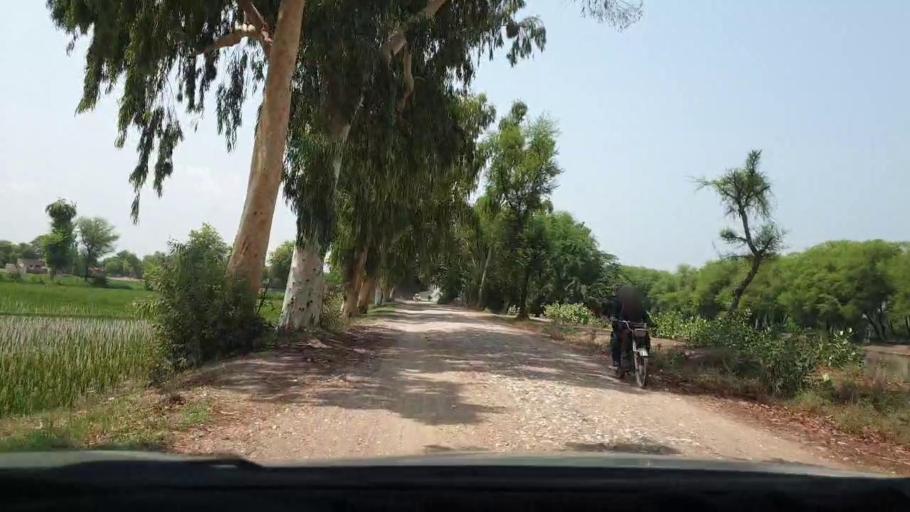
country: PK
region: Sindh
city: New Badah
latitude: 27.2985
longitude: 68.0885
